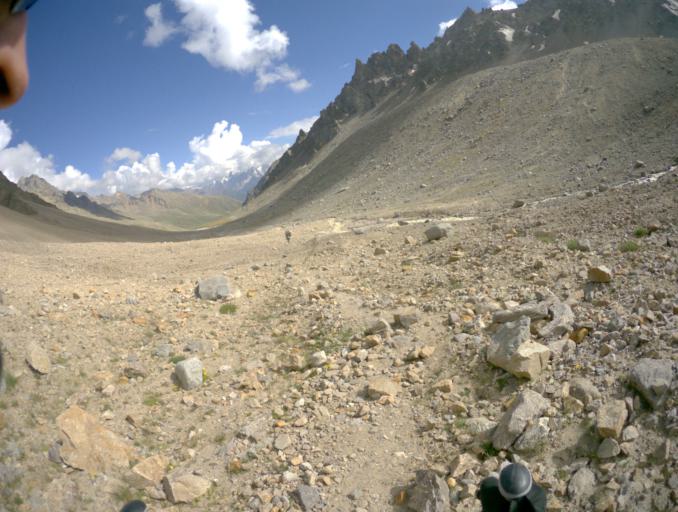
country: RU
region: Kabardino-Balkariya
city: Terskol
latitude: 43.3348
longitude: 42.5550
